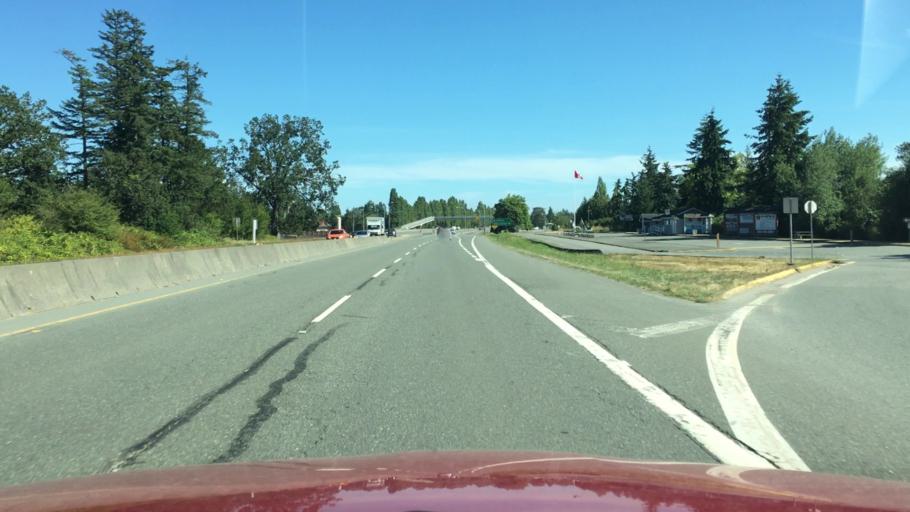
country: CA
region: British Columbia
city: North Saanich
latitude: 48.6656
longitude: -123.4206
